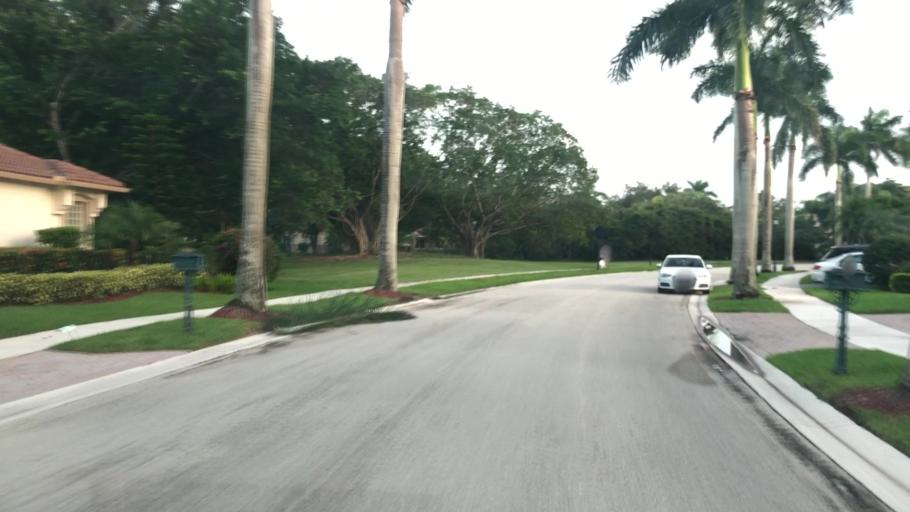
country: US
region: Florida
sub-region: Broward County
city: Weston
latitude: 26.0970
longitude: -80.4010
